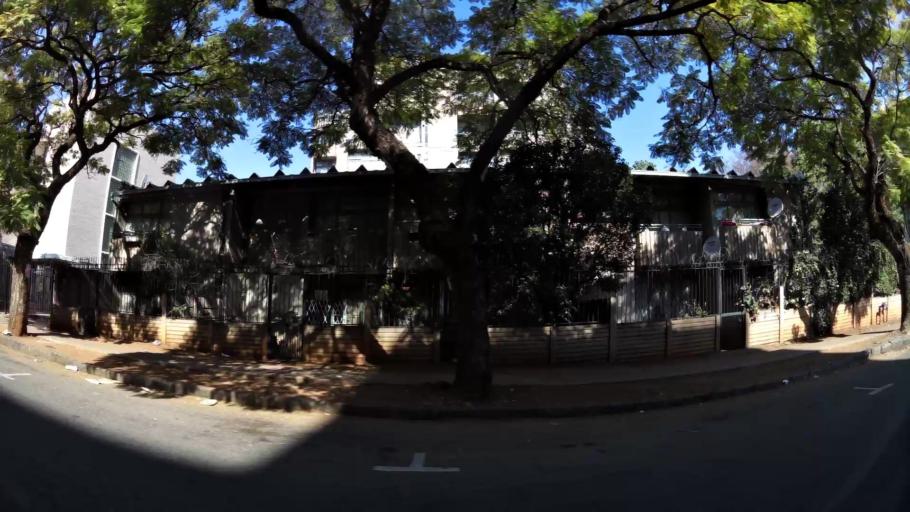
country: ZA
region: Gauteng
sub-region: City of Tshwane Metropolitan Municipality
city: Pretoria
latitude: -25.7464
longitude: 28.2107
